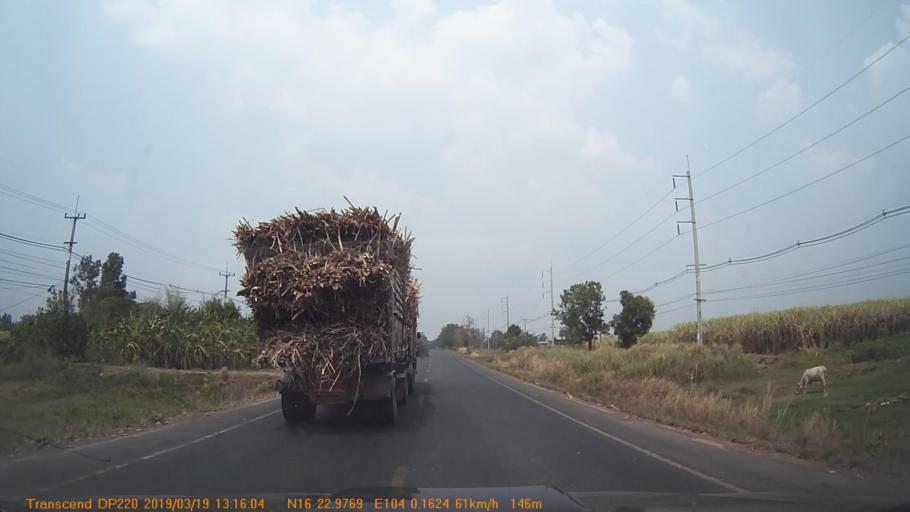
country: TH
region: Roi Et
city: Waeng
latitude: 16.3833
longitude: 104.0029
